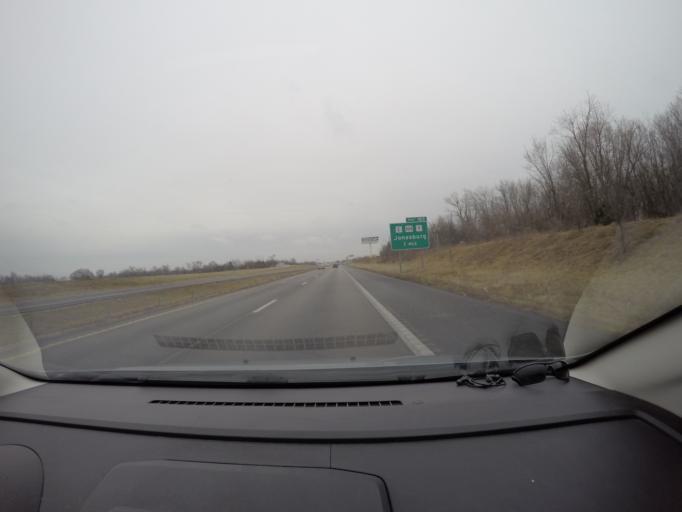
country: US
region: Missouri
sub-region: Warren County
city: Warrenton
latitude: 38.8640
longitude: -91.3245
